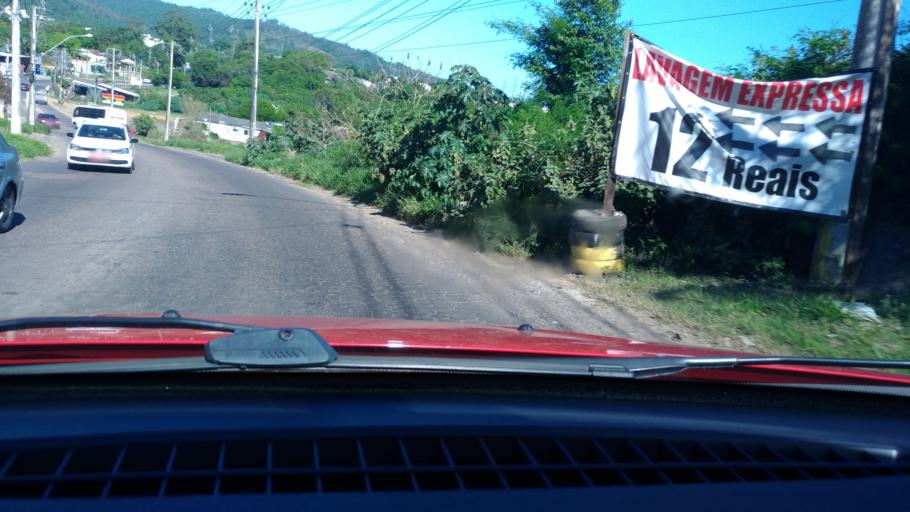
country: BR
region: Rio Grande do Sul
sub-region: Viamao
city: Viamao
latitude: -30.0456
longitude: -51.0834
